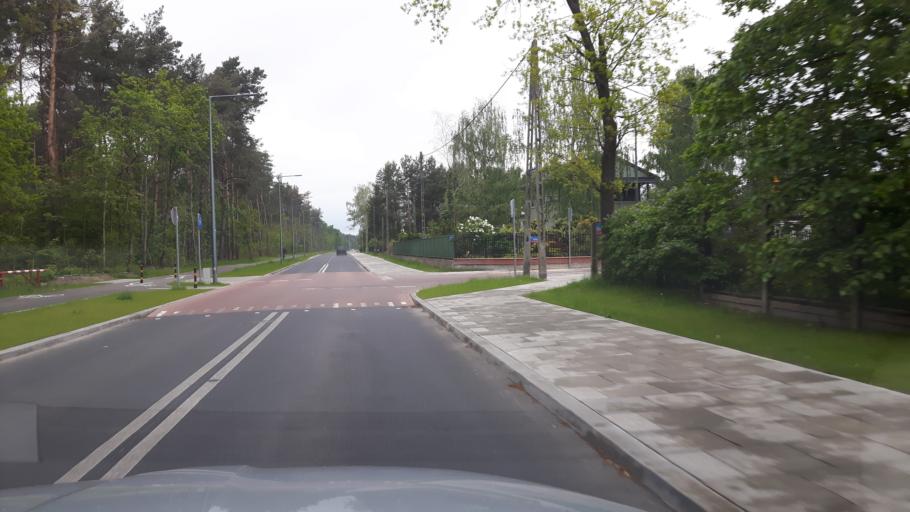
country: PL
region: Masovian Voivodeship
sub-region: Warszawa
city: Rembertow
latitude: 52.2620
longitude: 21.1506
